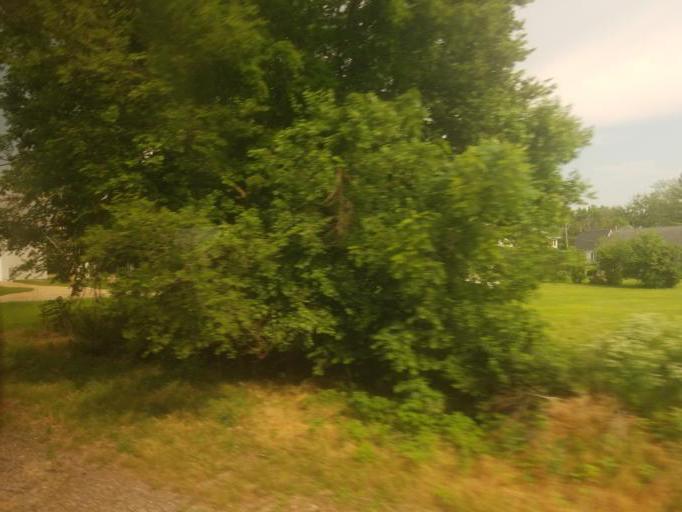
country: US
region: Illinois
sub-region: Bureau County
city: Princeton
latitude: 41.3638
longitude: -89.5845
